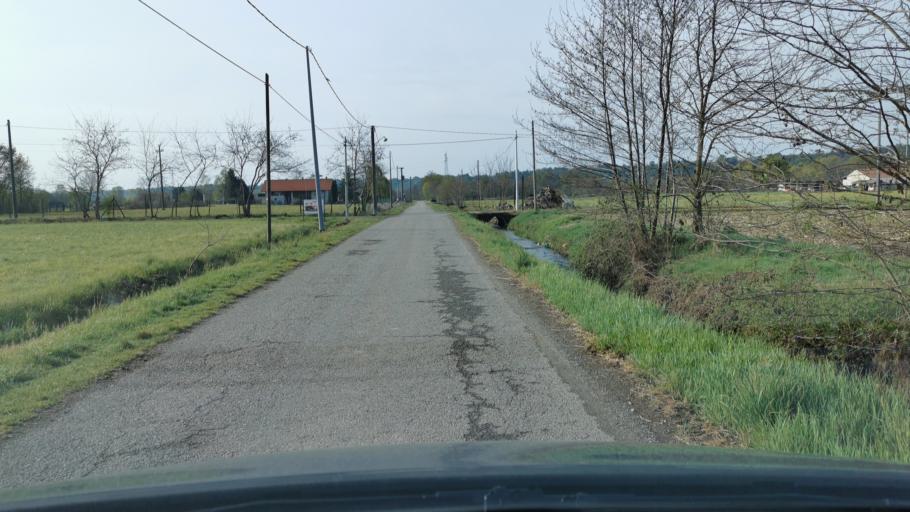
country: IT
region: Piedmont
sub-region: Provincia di Torino
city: Front
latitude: 45.2837
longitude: 7.6883
